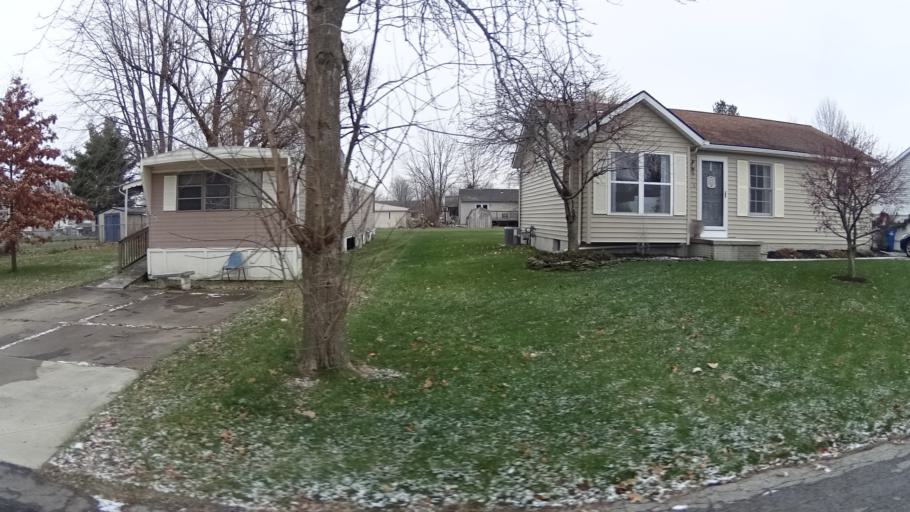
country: US
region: Ohio
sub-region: Lorain County
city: Lagrange
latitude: 41.2014
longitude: -82.1458
